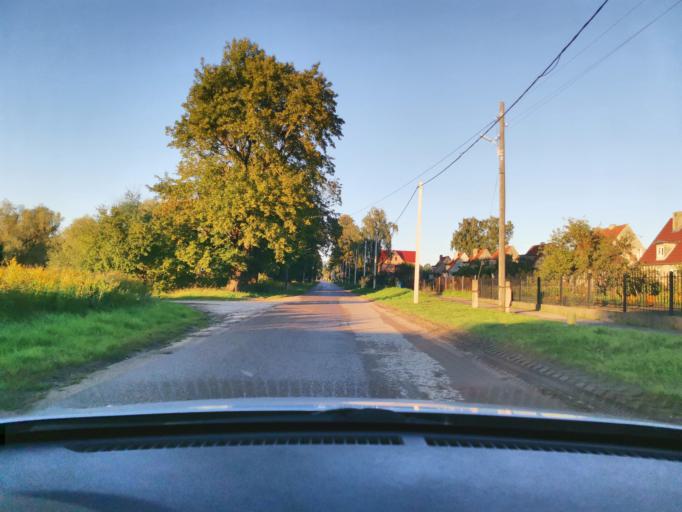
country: RU
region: Kaliningrad
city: Chernyakhovsk
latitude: 54.6536
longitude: 21.8197
